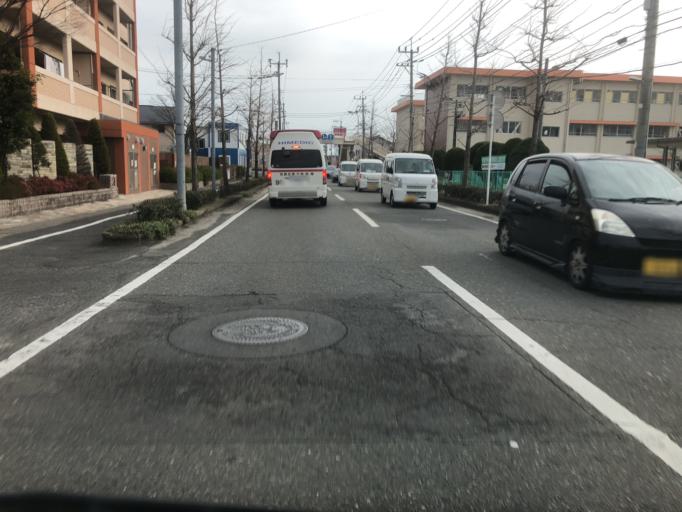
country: JP
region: Saga Prefecture
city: Saga-shi
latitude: 33.2751
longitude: 130.2707
